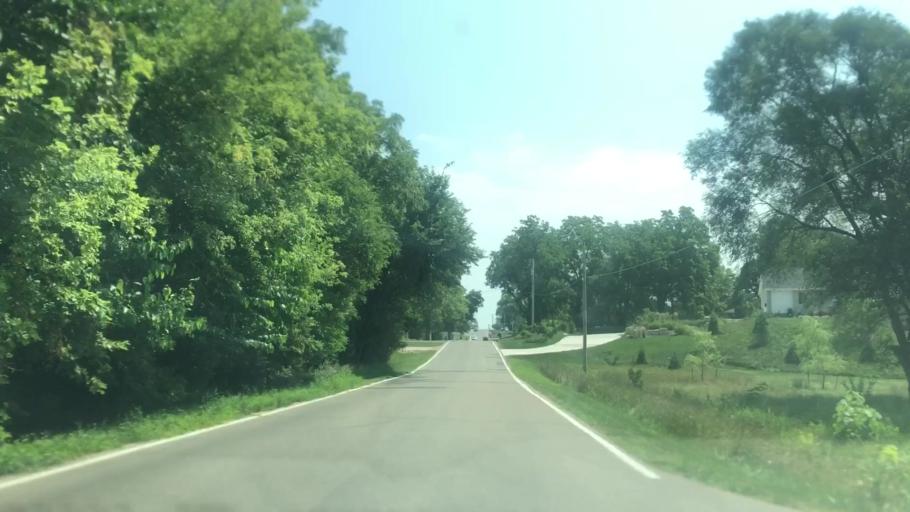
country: US
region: Iowa
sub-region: Marshall County
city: Marshalltown
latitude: 42.0286
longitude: -92.9383
